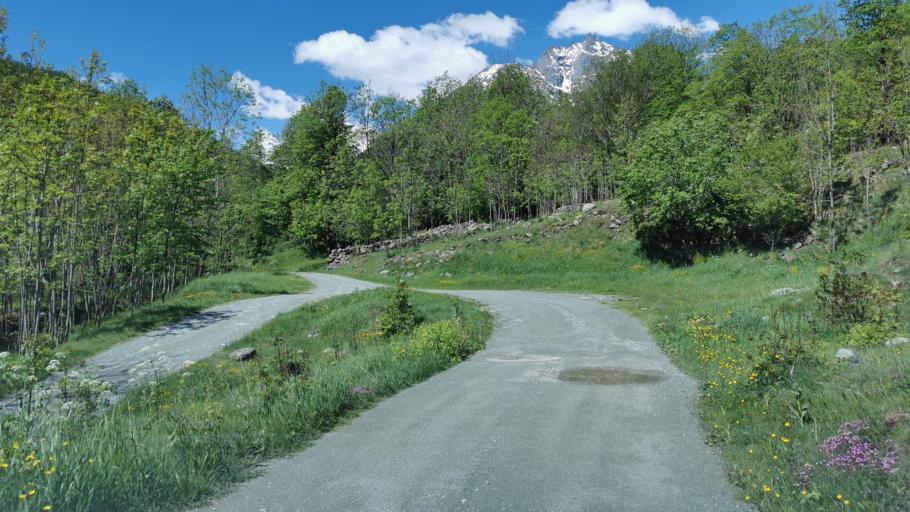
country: IT
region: Piedmont
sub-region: Provincia di Torino
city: Usseglio
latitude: 45.2331
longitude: 7.2299
